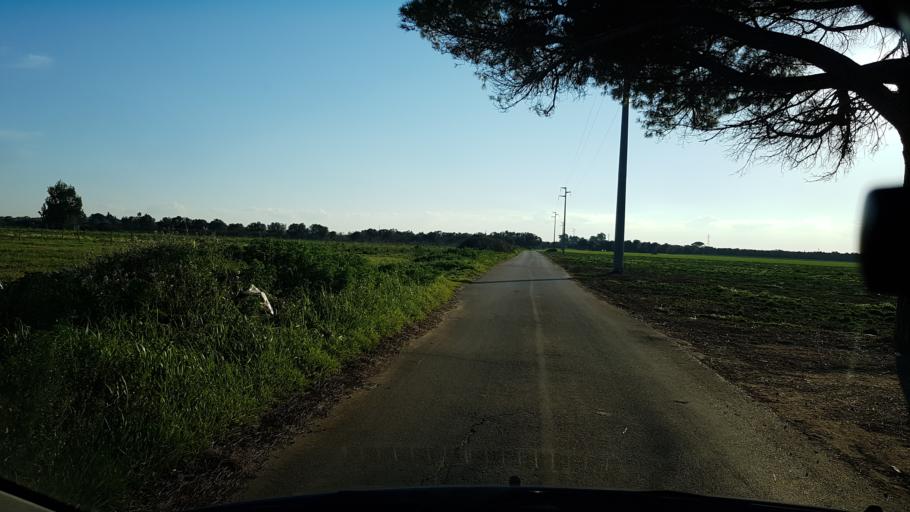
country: IT
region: Apulia
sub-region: Provincia di Brindisi
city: Brindisi
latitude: 40.5821
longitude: 17.8826
